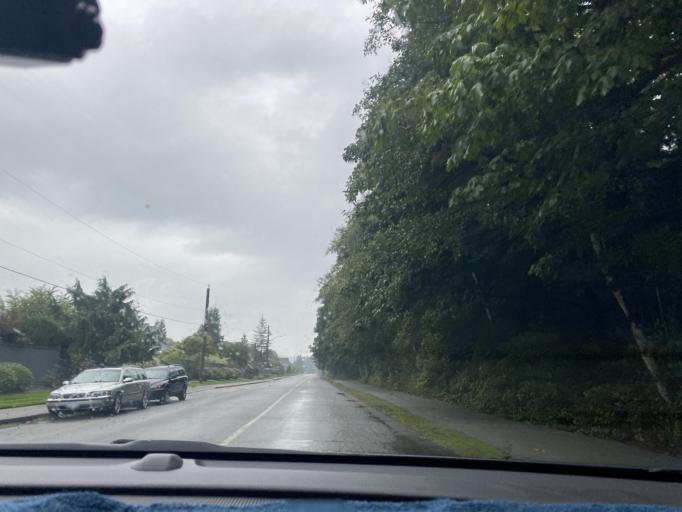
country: CA
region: British Columbia
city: Agassiz
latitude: 49.2896
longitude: -121.7775
